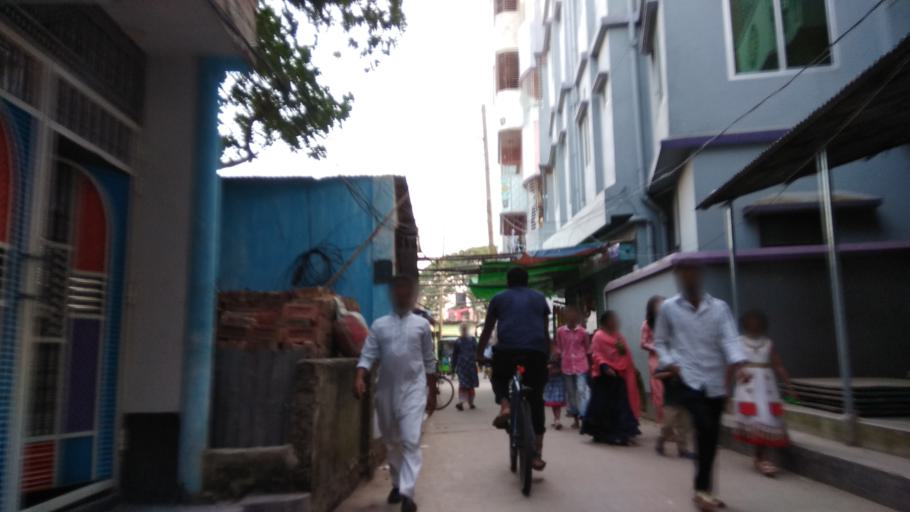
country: BD
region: Dhaka
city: Azimpur
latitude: 23.7995
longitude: 90.3393
